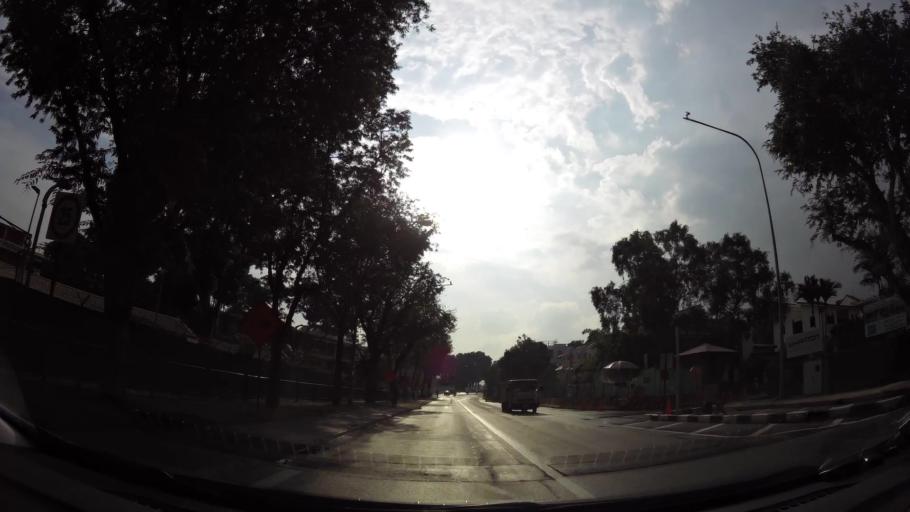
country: SG
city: Singapore
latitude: 1.3193
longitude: 103.9543
